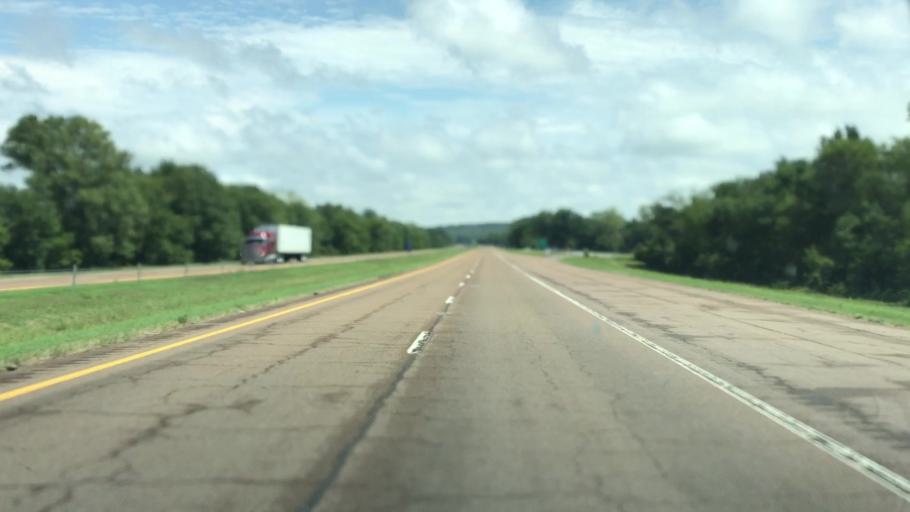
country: US
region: Tennessee
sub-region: Dyer County
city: Dyersburg
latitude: 36.0804
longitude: -89.5279
